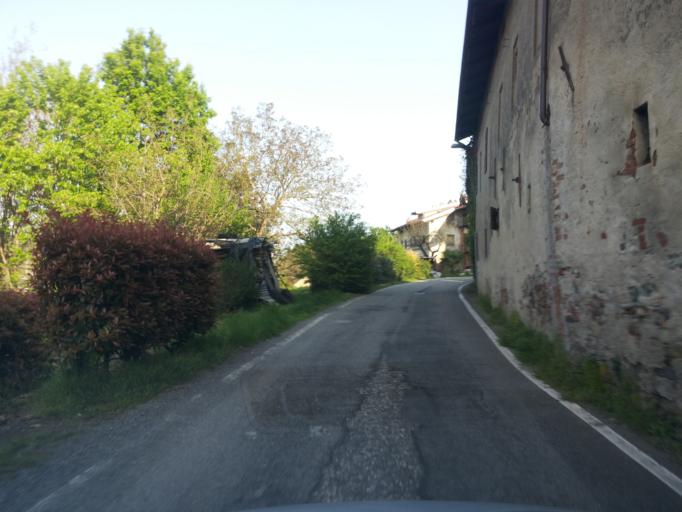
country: IT
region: Piedmont
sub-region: Provincia di Torino
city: Azeglio
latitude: 45.4264
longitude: 7.9959
